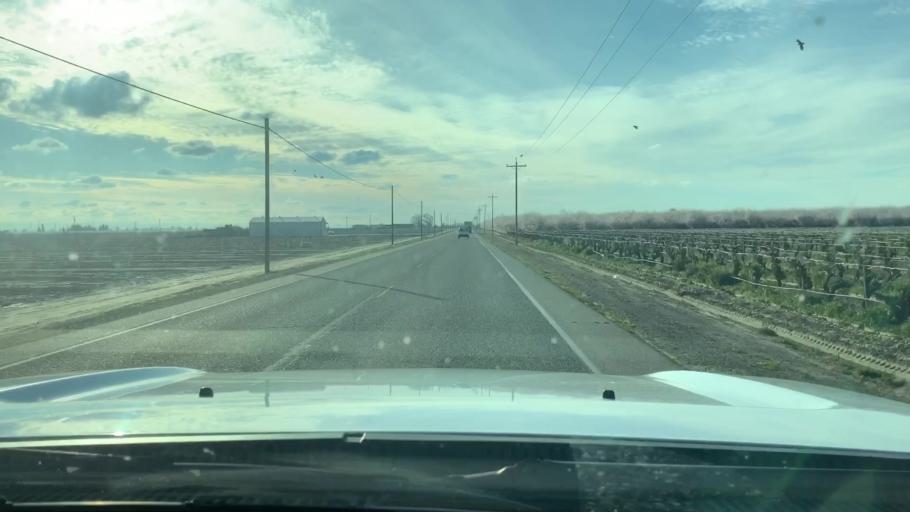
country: US
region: California
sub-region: Fresno County
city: Easton
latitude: 36.6053
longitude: -119.7663
